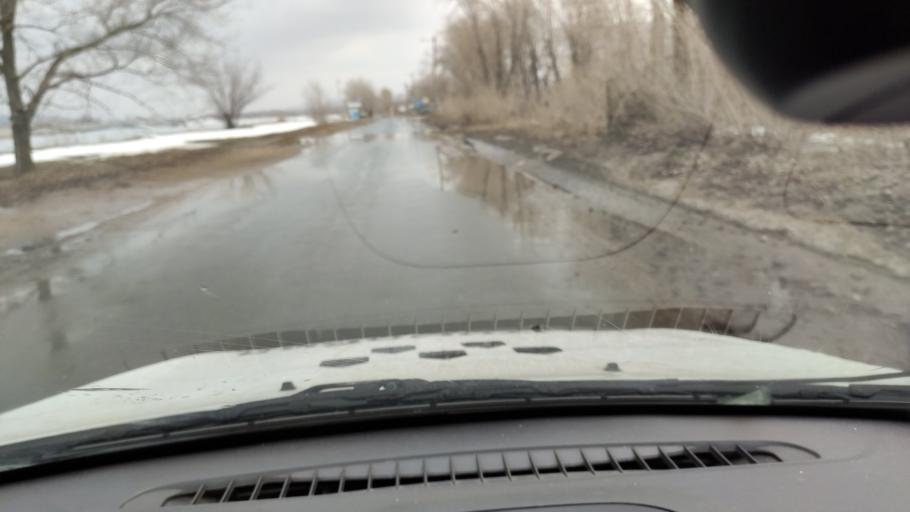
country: RU
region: Samara
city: Zhigulevsk
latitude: 53.4581
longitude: 49.5331
